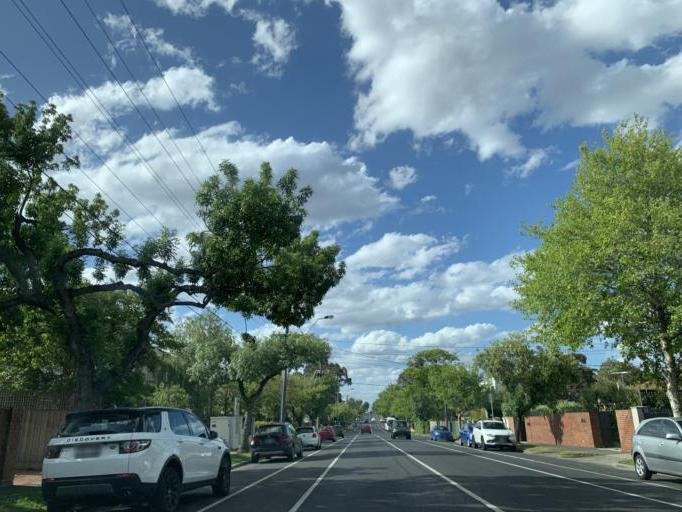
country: AU
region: Victoria
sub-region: Bayside
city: Hampton
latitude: -37.9276
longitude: 145.0043
